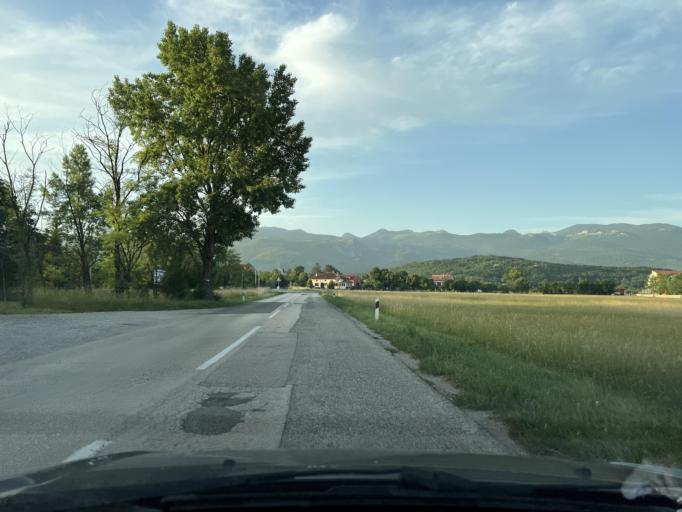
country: HR
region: Primorsko-Goranska
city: Drazice
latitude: 45.3827
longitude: 14.4703
